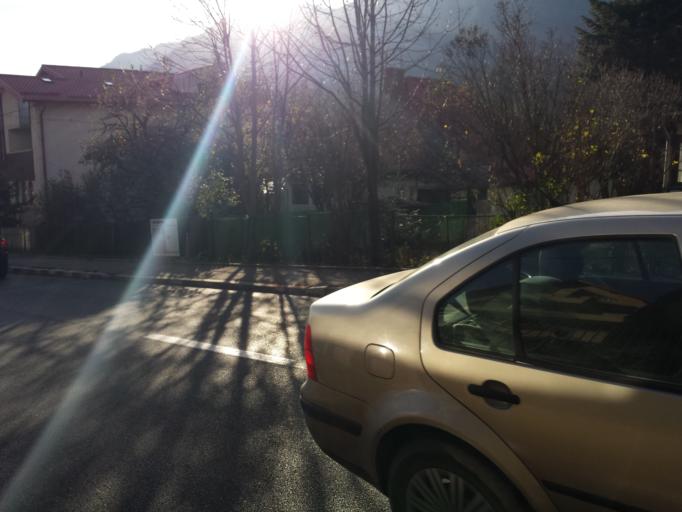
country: RO
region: Prahova
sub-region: Oras Busteni
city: Busteni
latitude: 45.4034
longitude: 25.5402
